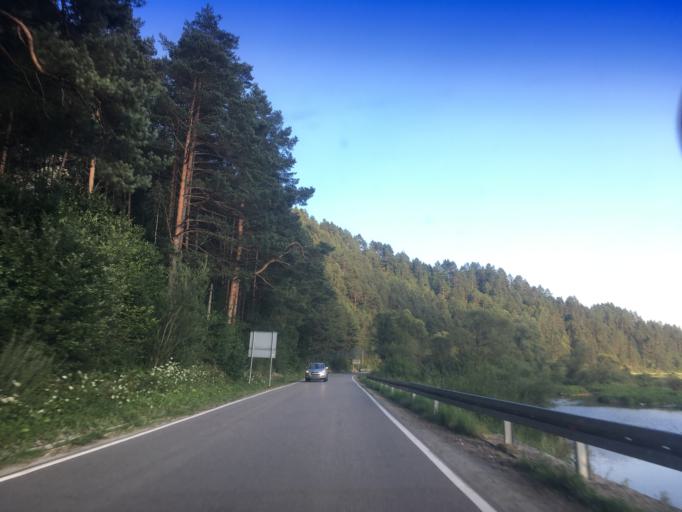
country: PL
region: Lesser Poland Voivodeship
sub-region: Powiat nowotarski
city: Krosnica
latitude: 49.4065
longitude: 20.3789
